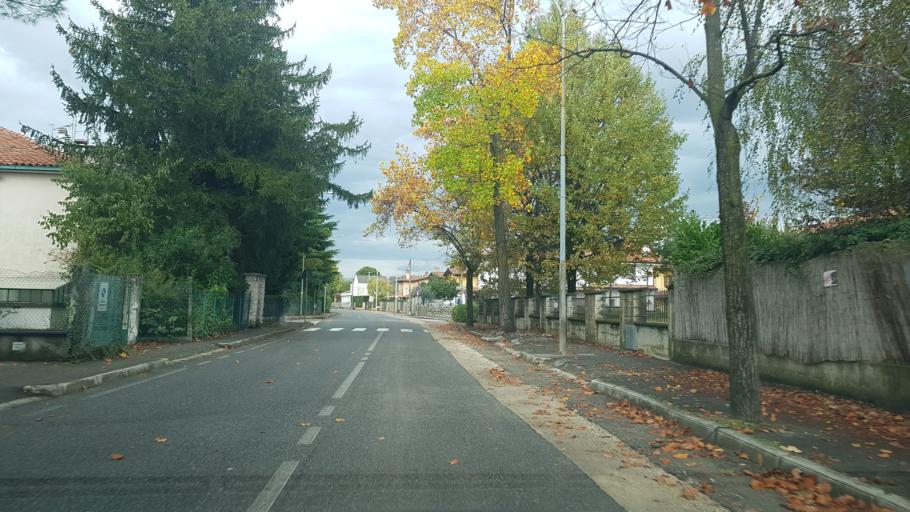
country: IT
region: Friuli Venezia Giulia
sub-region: Provincia di Gorizia
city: Ronchi dei Legionari
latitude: 45.8262
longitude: 13.5119
